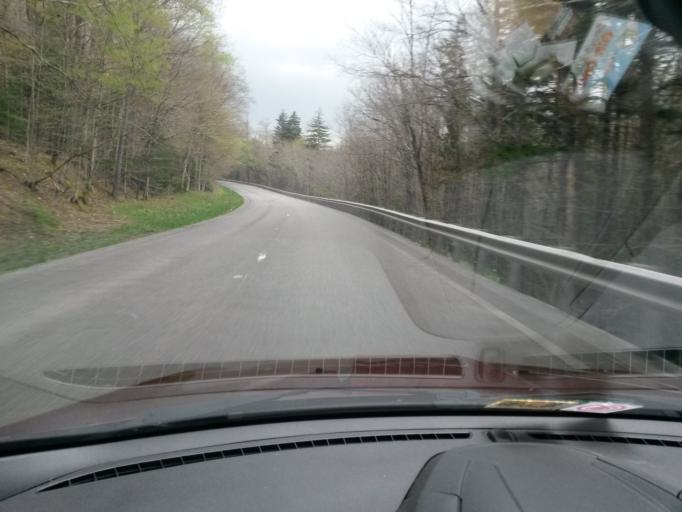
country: US
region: West Virginia
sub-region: Randolph County
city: Elkins
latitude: 38.6284
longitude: -79.9022
